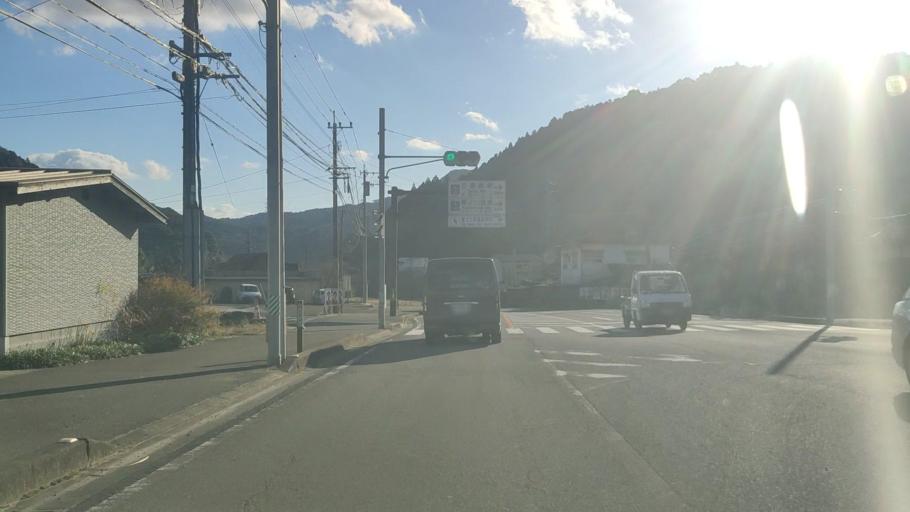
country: JP
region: Saga Prefecture
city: Saga-shi
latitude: 33.3521
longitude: 130.2484
